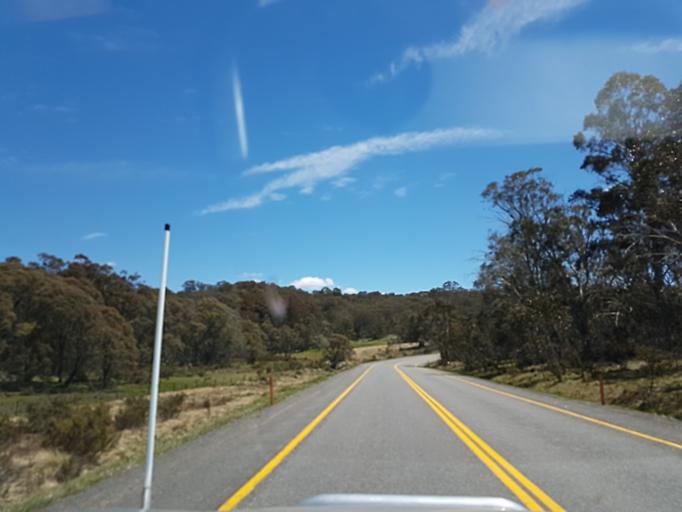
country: AU
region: Victoria
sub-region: Alpine
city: Mount Beauty
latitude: -37.0475
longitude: 147.3154
